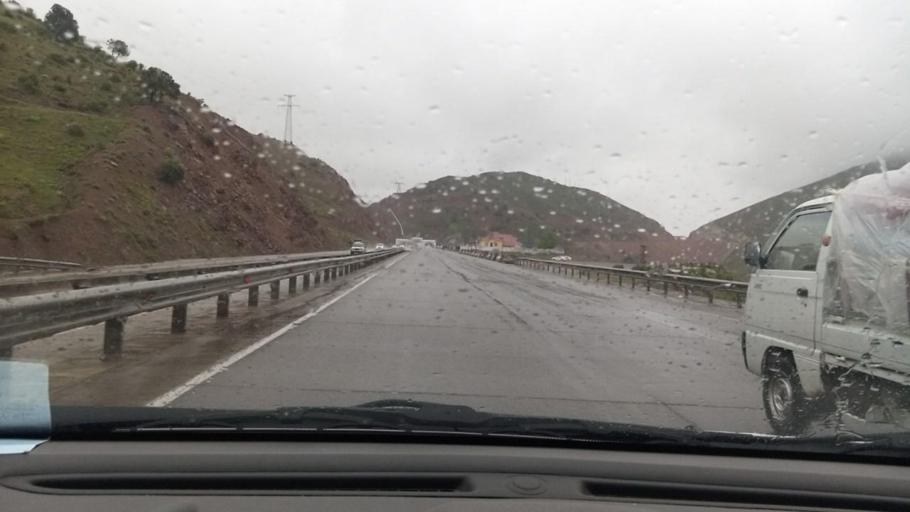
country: UZ
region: Toshkent
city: Angren
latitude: 41.0845
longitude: 70.5398
